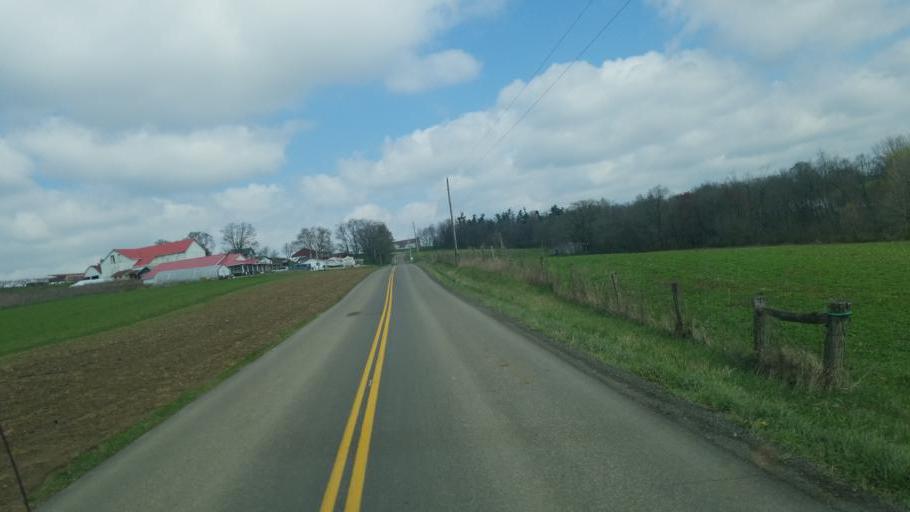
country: US
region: Ohio
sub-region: Holmes County
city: Millersburg
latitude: 40.6342
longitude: -81.8452
